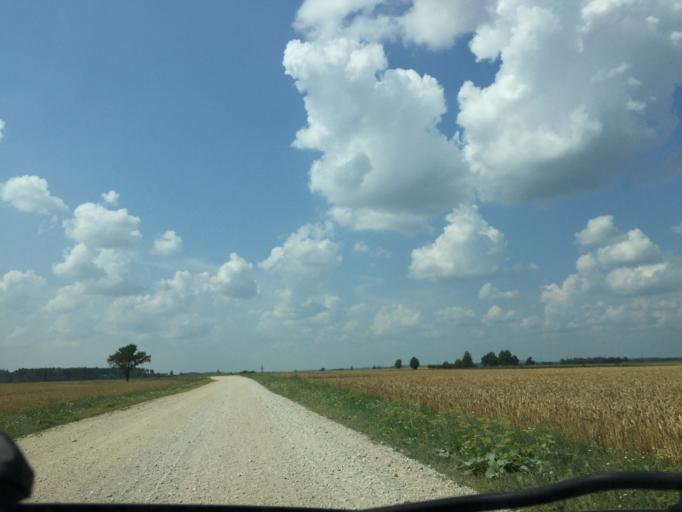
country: LT
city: Zagare
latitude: 56.3955
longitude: 23.2138
